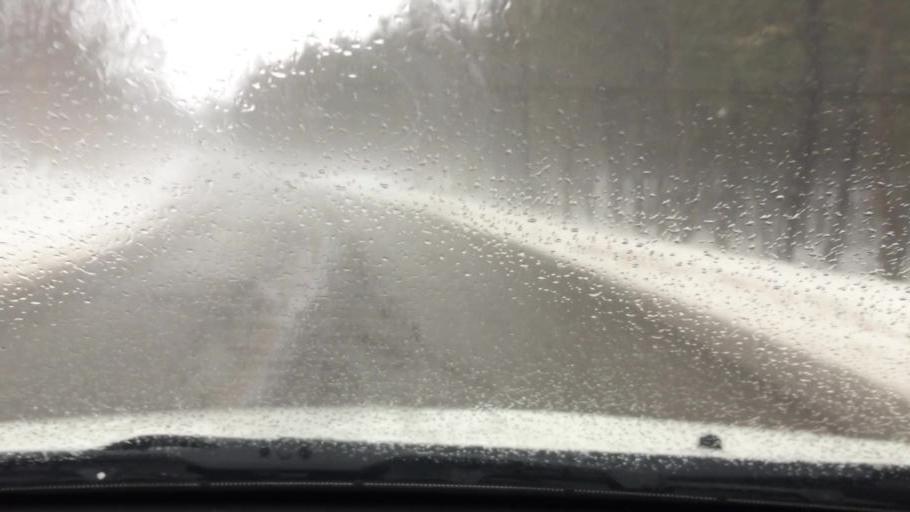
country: US
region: Michigan
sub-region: Charlevoix County
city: East Jordan
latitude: 45.1024
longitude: -85.1398
